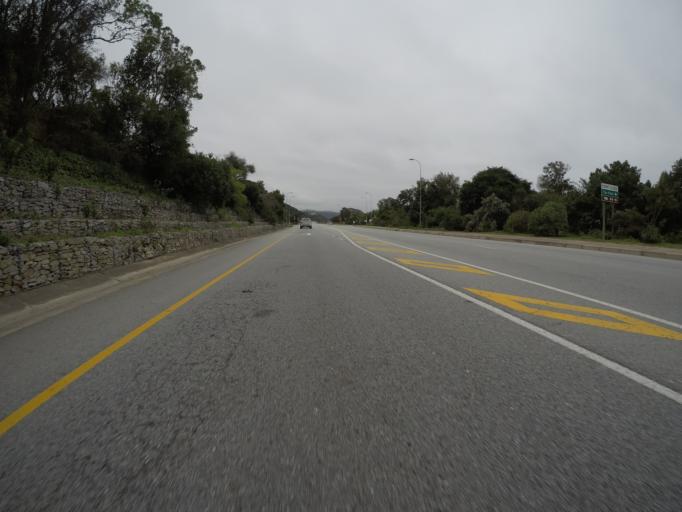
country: ZA
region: Western Cape
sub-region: Eden District Municipality
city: Knysna
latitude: -34.0387
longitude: 23.0163
